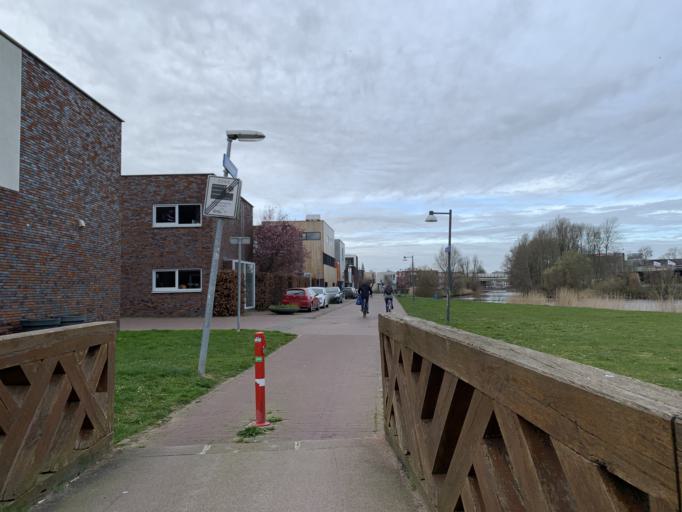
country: NL
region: Groningen
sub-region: Gemeente Groningen
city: Oosterpark
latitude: 53.2069
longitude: 6.5859
